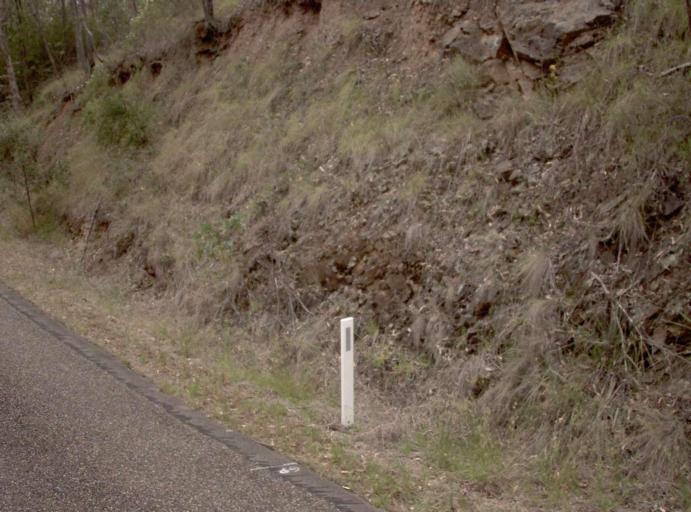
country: AU
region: Victoria
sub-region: East Gippsland
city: Bairnsdale
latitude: -37.4964
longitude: 147.1999
